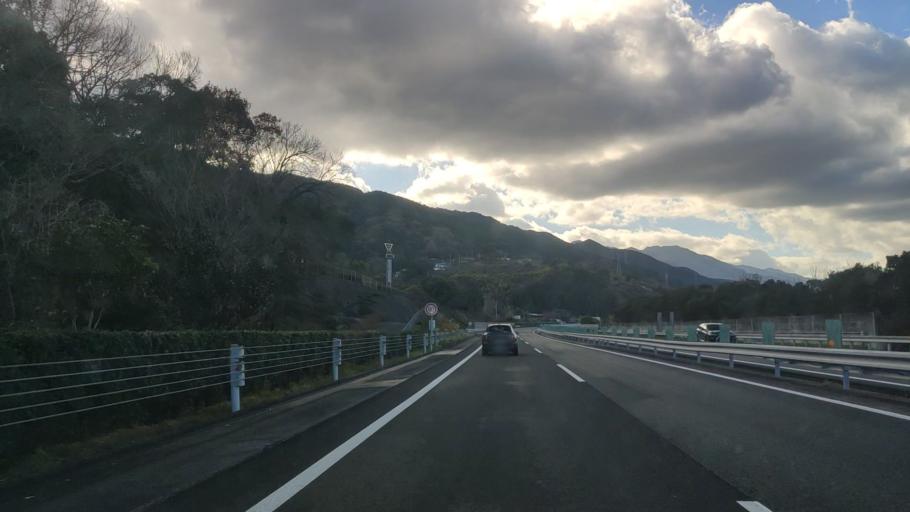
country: JP
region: Ehime
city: Kawanoecho
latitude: 33.9731
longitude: 133.5577
